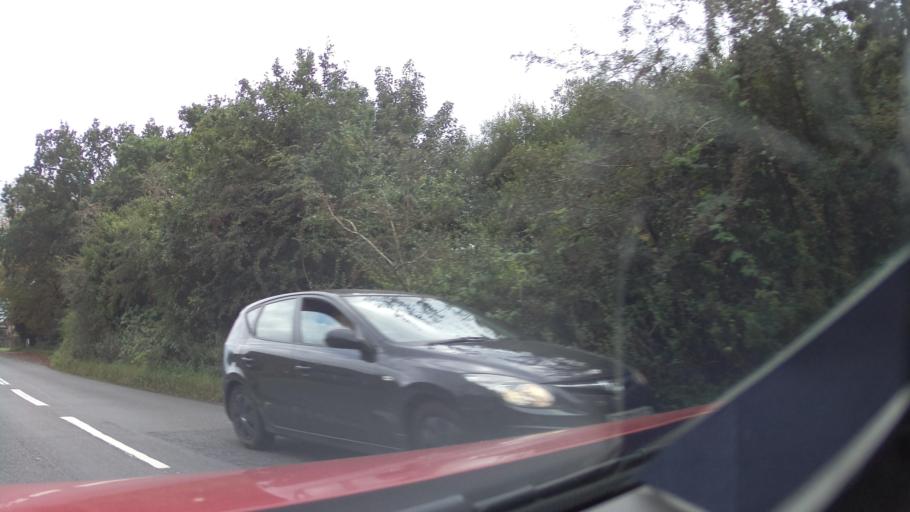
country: GB
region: England
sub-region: Solihull
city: Cheswick Green
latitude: 52.3594
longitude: -1.7799
